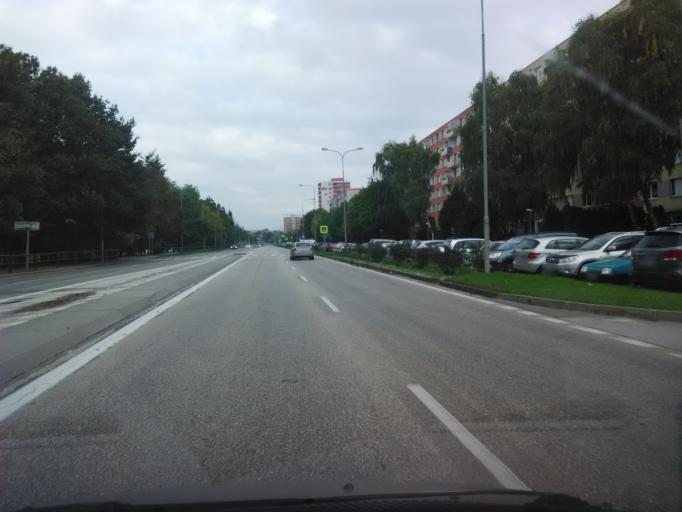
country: SK
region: Nitriansky
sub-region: Okres Nitra
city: Nitra
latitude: 48.3113
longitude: 18.0999
